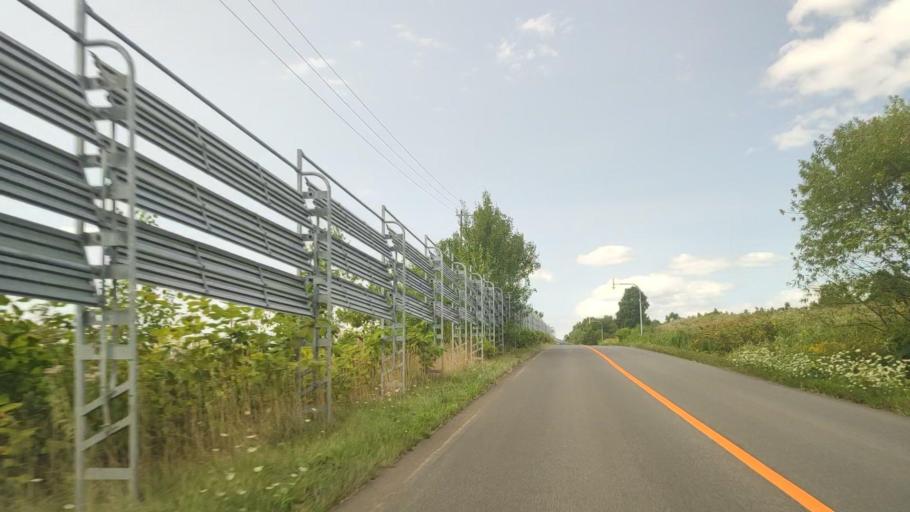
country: JP
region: Hokkaido
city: Nayoro
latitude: 44.2465
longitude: 142.4156
